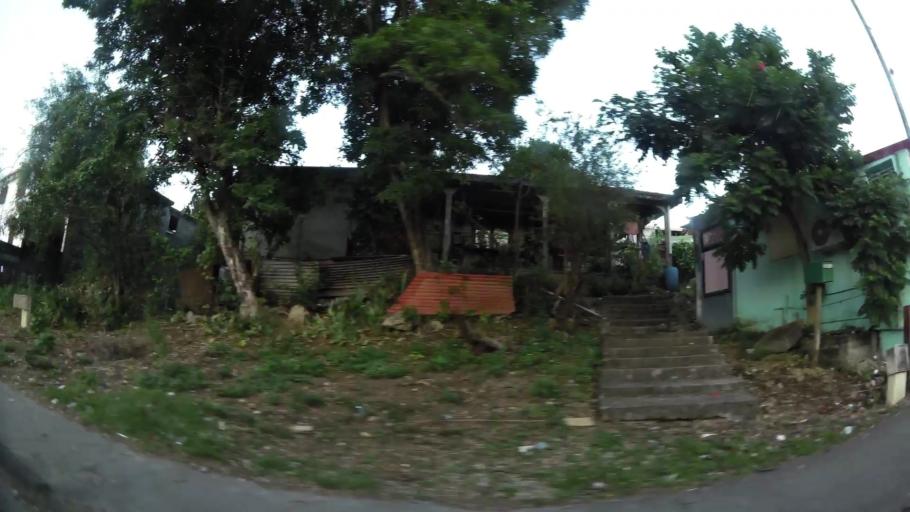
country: GP
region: Guadeloupe
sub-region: Guadeloupe
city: Les Abymes
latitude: 16.2740
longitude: -61.4997
